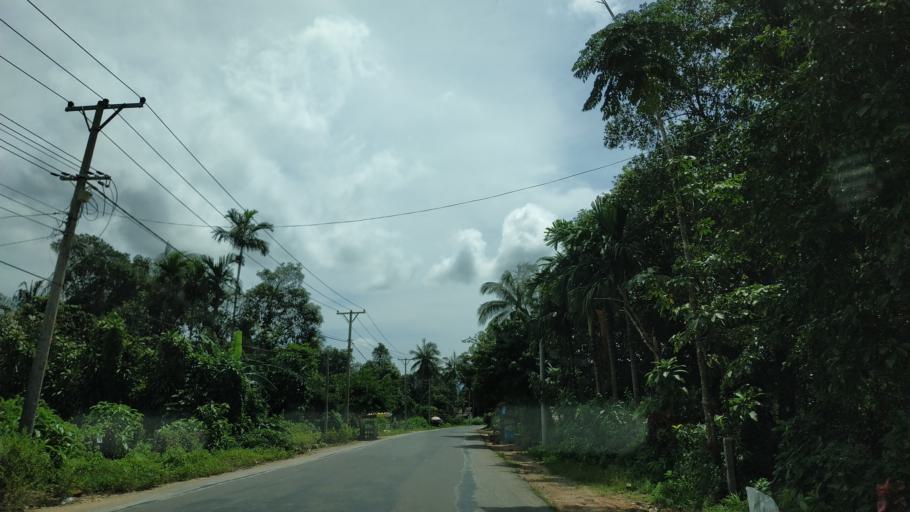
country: MM
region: Tanintharyi
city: Dawei
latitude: 14.1285
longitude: 98.1228
